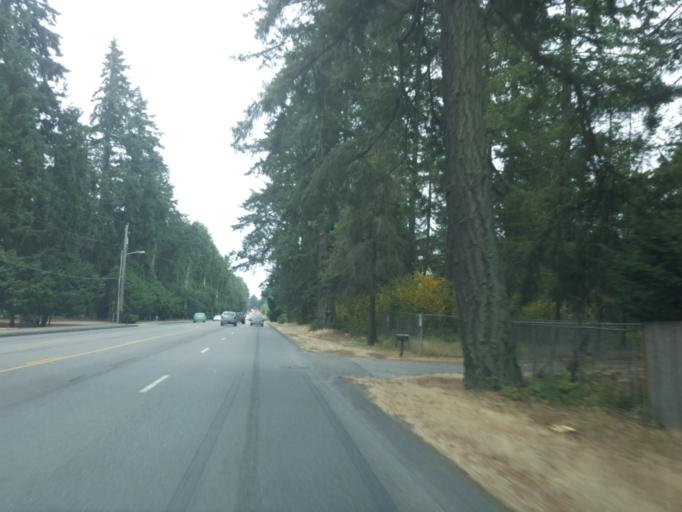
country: US
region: Washington
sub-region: Pierce County
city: Parkland
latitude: 47.1353
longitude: -122.4590
